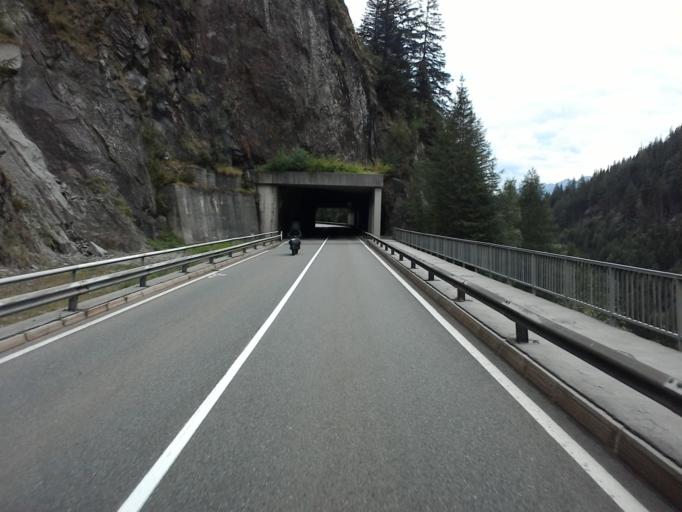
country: AT
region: Tyrol
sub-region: Politischer Bezirk Lienz
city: Matrei in Osttirol
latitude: 47.0264
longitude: 12.5208
